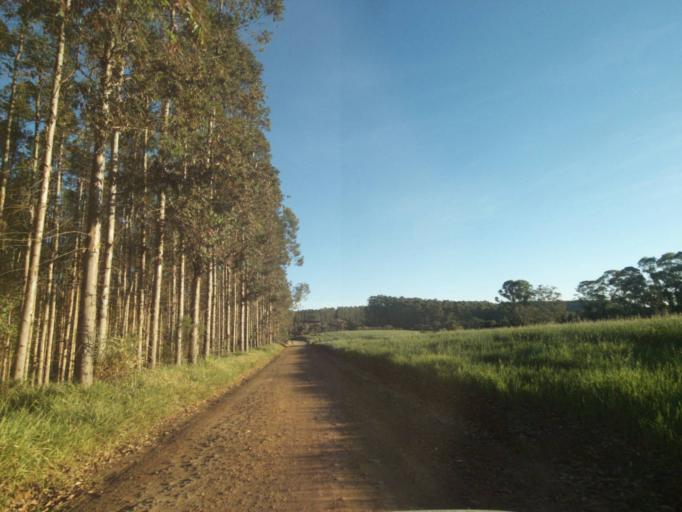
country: BR
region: Parana
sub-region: Telemaco Borba
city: Telemaco Borba
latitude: -24.4868
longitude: -50.5931
